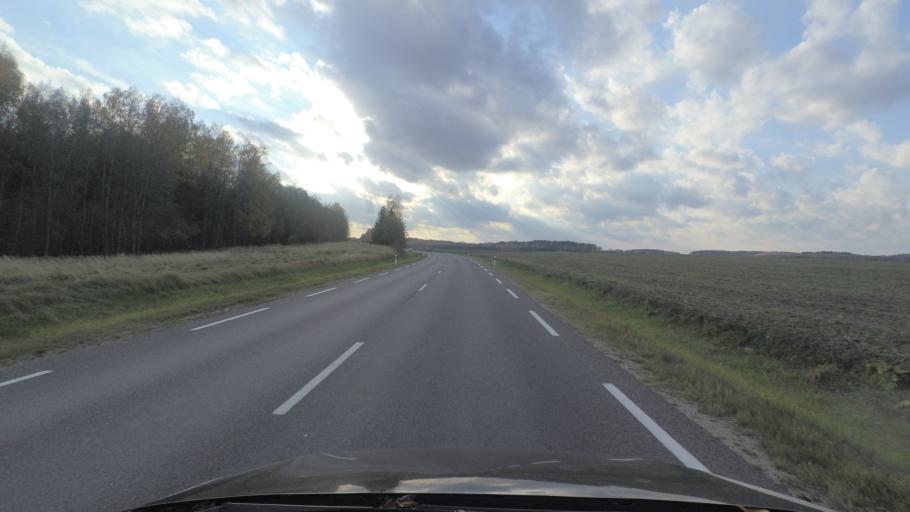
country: LT
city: Svencionys
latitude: 55.1036
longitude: 26.0925
